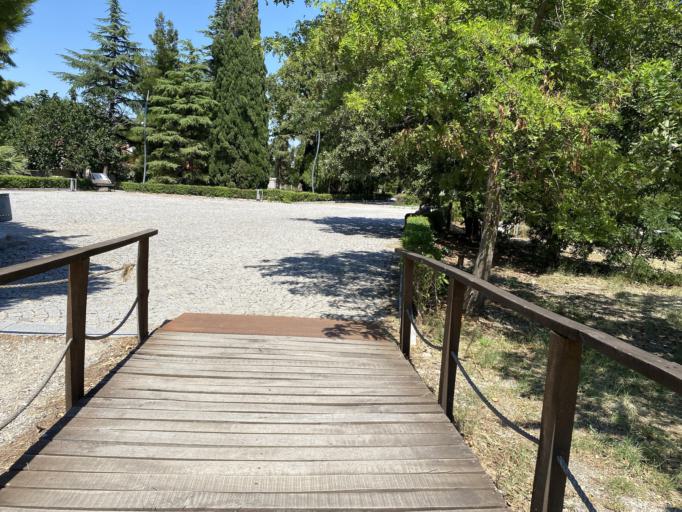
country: TR
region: Canakkale
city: Intepe
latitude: 39.9568
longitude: 26.2397
